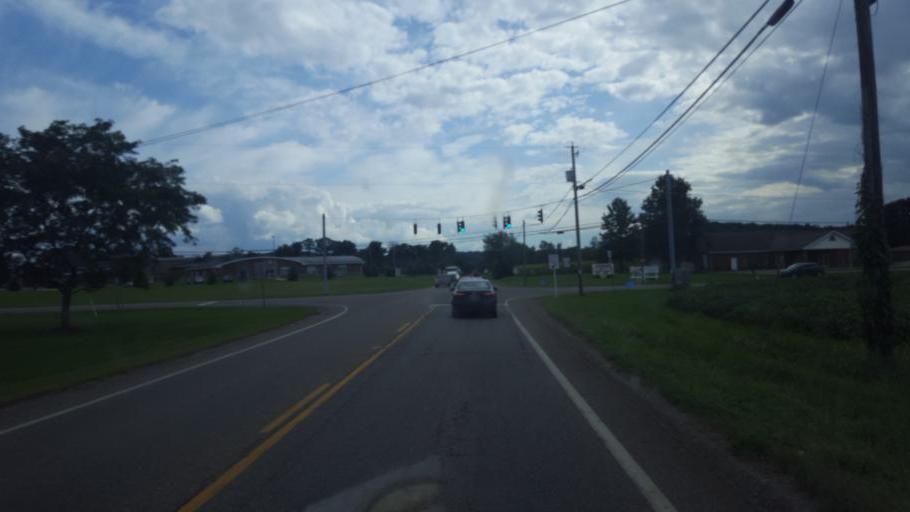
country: US
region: Ohio
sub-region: Carroll County
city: Lake Mohawk
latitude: 40.6393
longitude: -81.3559
